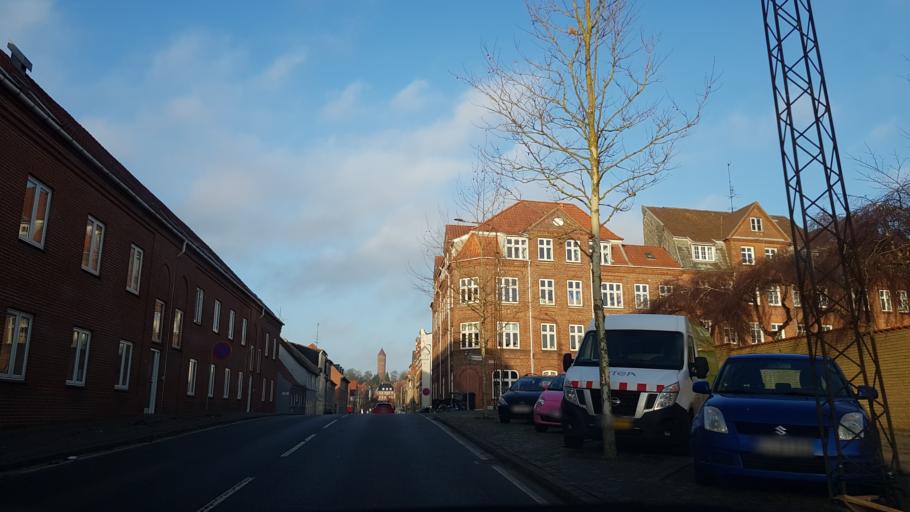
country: DK
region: South Denmark
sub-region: Haderslev Kommune
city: Haderslev
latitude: 55.2496
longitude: 9.4944
